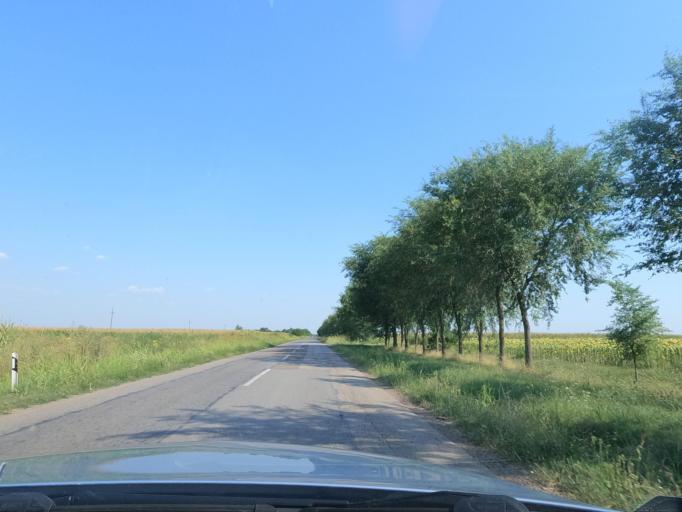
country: RS
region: Autonomna Pokrajina Vojvodina
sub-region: Juznobacki Okrug
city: Becej
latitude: 45.6499
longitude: 19.9772
